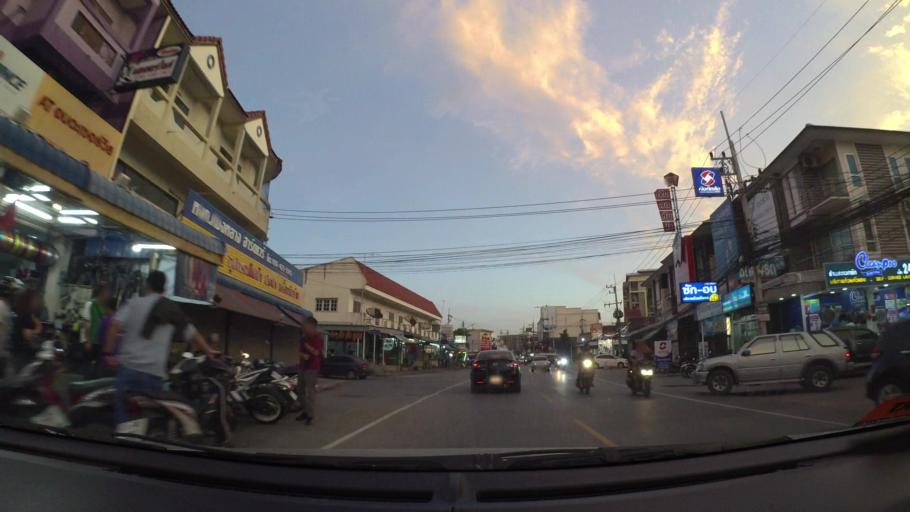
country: TH
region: Chon Buri
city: Chon Buri
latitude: 13.4183
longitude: 101.0002
